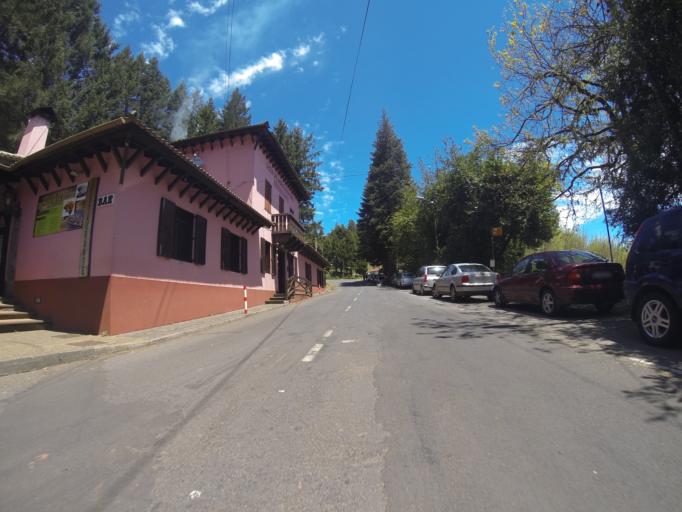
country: PT
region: Madeira
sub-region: Funchal
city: Nossa Senhora do Monte
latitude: 32.7124
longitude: -16.8937
